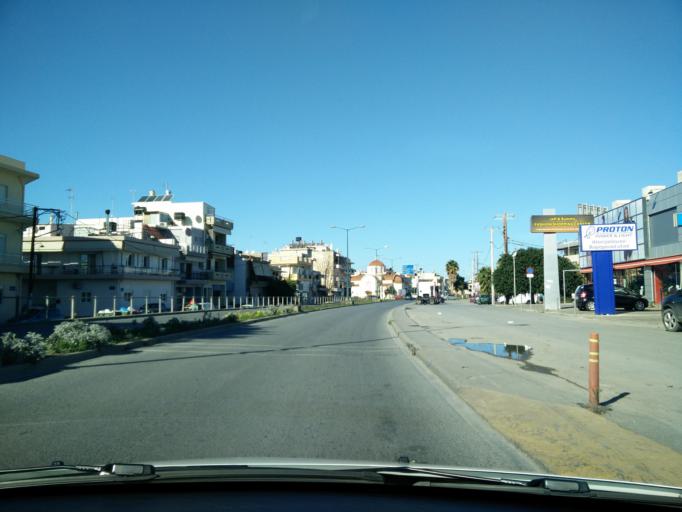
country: GR
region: Crete
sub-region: Nomos Irakleiou
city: Nea Alikarnassos
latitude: 35.3378
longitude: 25.1542
